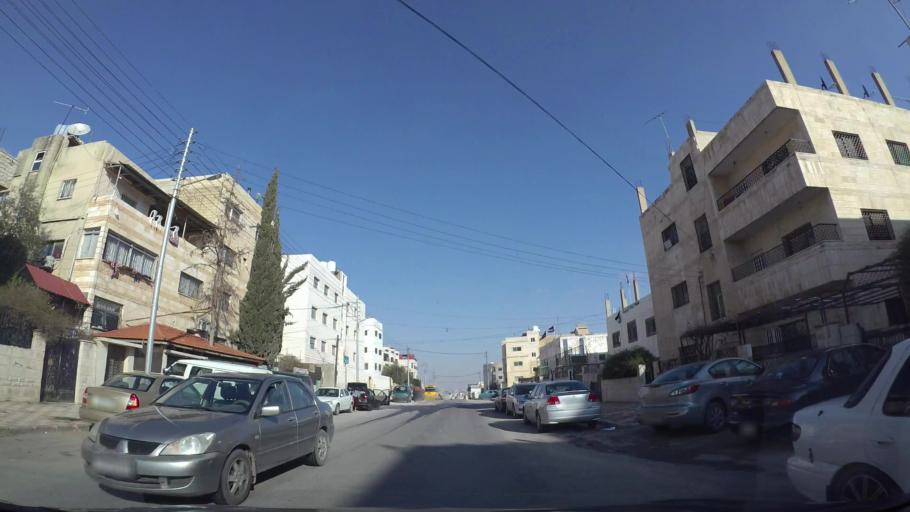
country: JO
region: Amman
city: Amman
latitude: 31.9799
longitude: 35.9587
